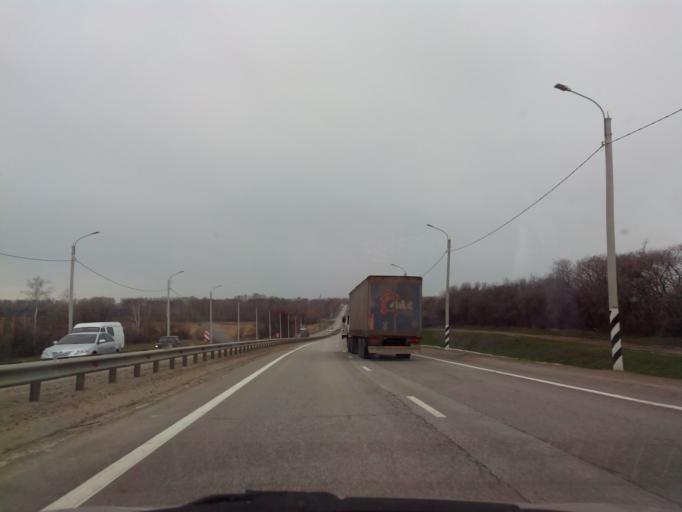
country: RU
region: Tambov
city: Selezni
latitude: 52.7440
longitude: 41.2009
